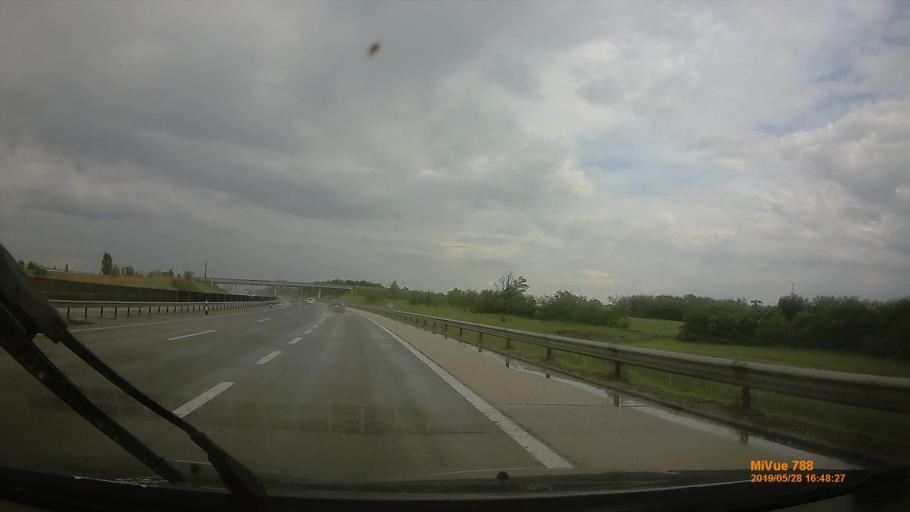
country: HU
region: Pest
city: Nagytarcsa
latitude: 47.5101
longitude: 19.2707
